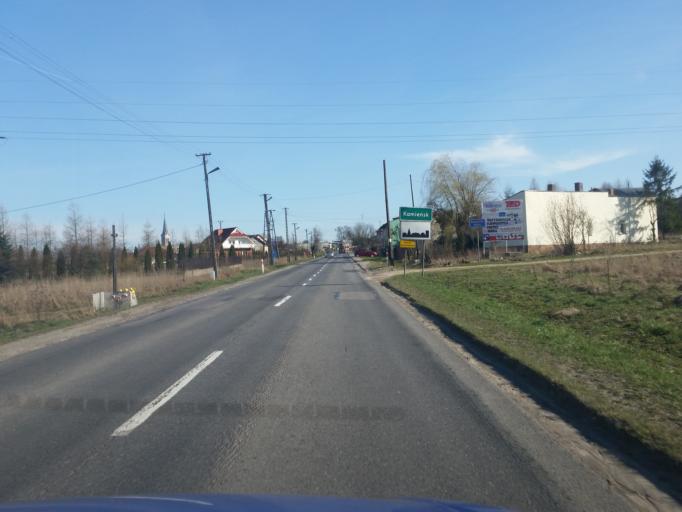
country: PL
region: Lodz Voivodeship
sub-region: Powiat radomszczanski
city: Kamiensk
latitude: 51.2081
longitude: 19.4911
